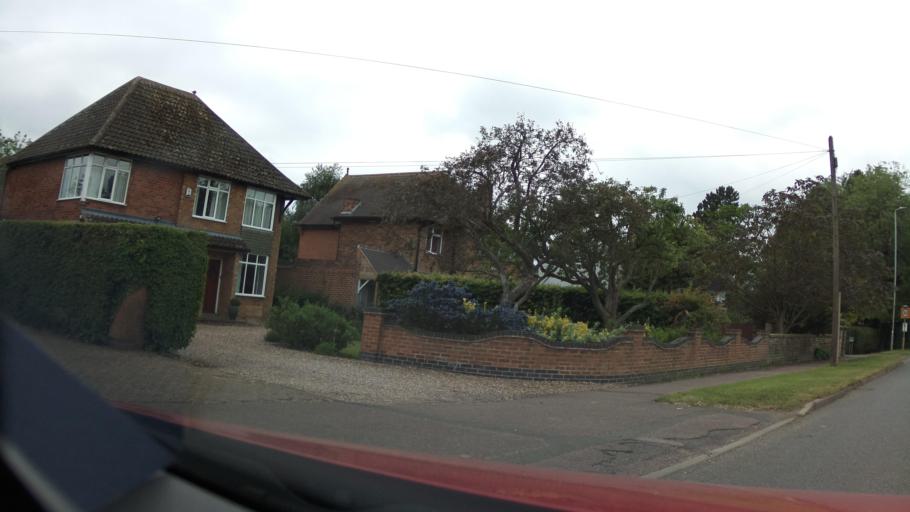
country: GB
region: England
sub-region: Leicestershire
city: Melton Mowbray
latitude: 52.7507
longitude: -0.8738
